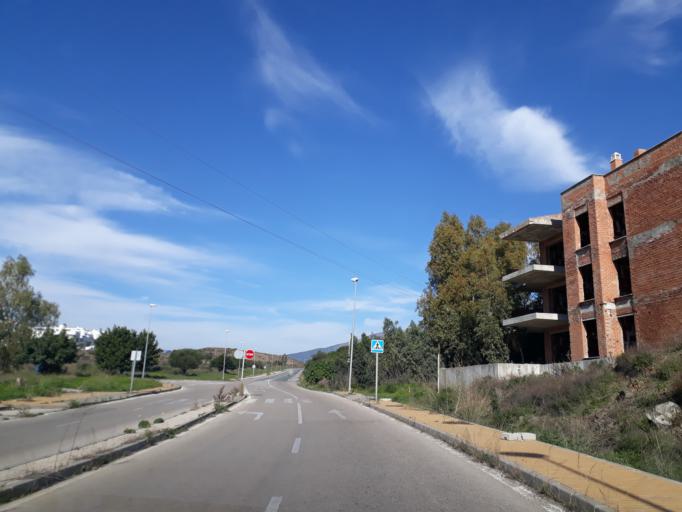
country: ES
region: Andalusia
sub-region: Provincia de Malaga
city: Fuengirola
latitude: 36.5261
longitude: -4.6858
